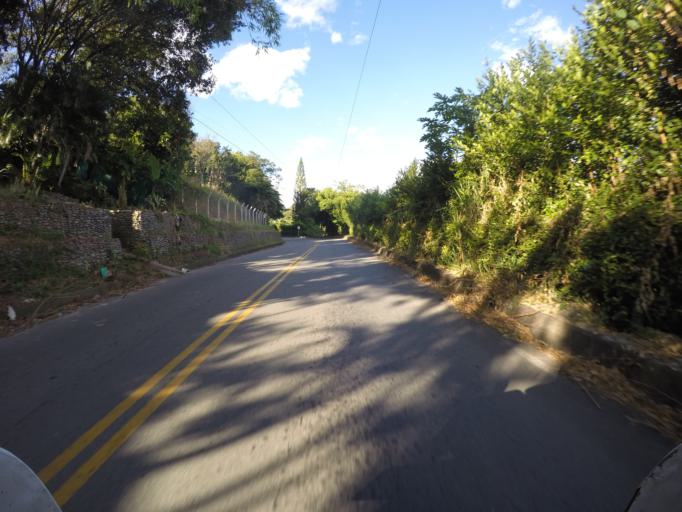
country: CO
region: Valle del Cauca
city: Alcala
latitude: 4.7049
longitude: -75.8468
